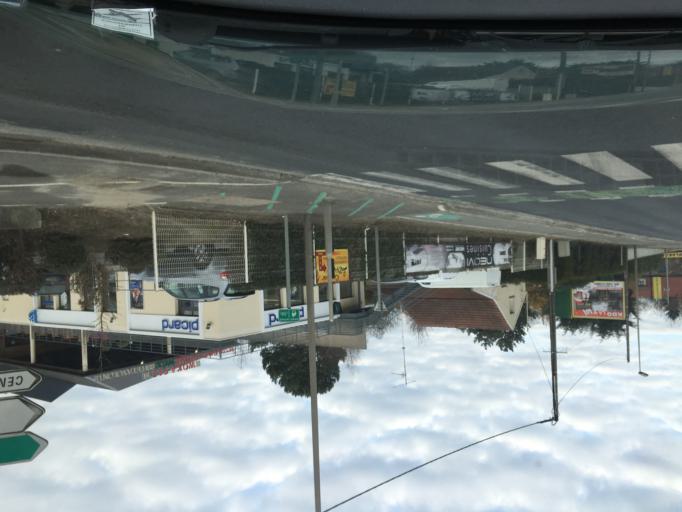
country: FR
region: Centre
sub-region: Departement du Loiret
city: Saran
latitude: 47.9547
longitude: 1.8912
